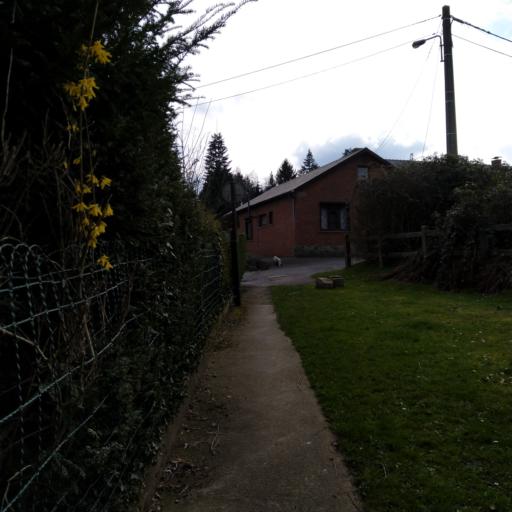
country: BE
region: Wallonia
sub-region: Province du Hainaut
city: Mons
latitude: 50.5094
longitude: 4.0001
